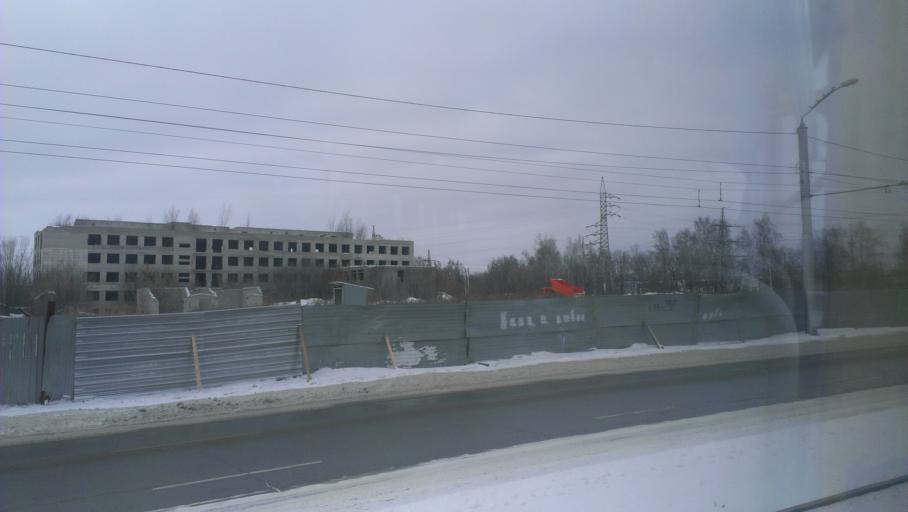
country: RU
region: Altai Krai
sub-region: Gorod Barnaulskiy
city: Barnaul
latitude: 53.3849
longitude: 83.7130
